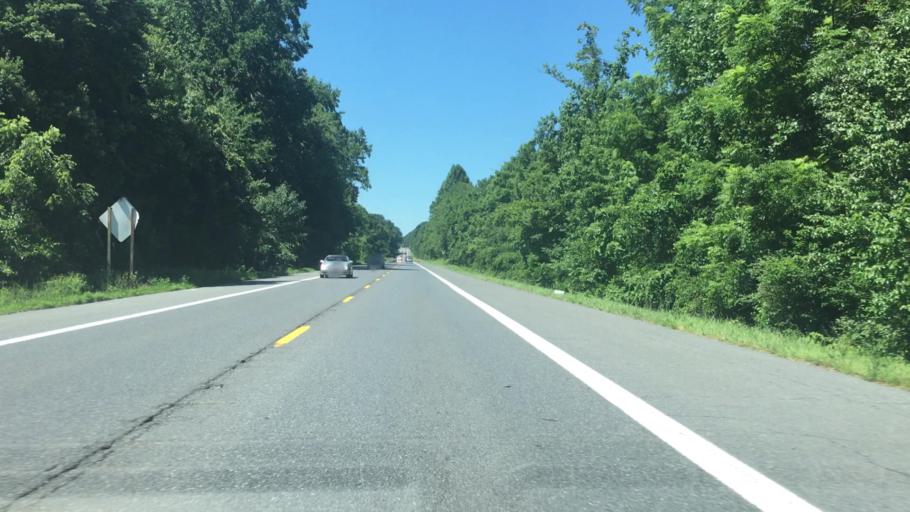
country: US
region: Maryland
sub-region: Howard County
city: Highland
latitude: 39.2383
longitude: -76.9753
